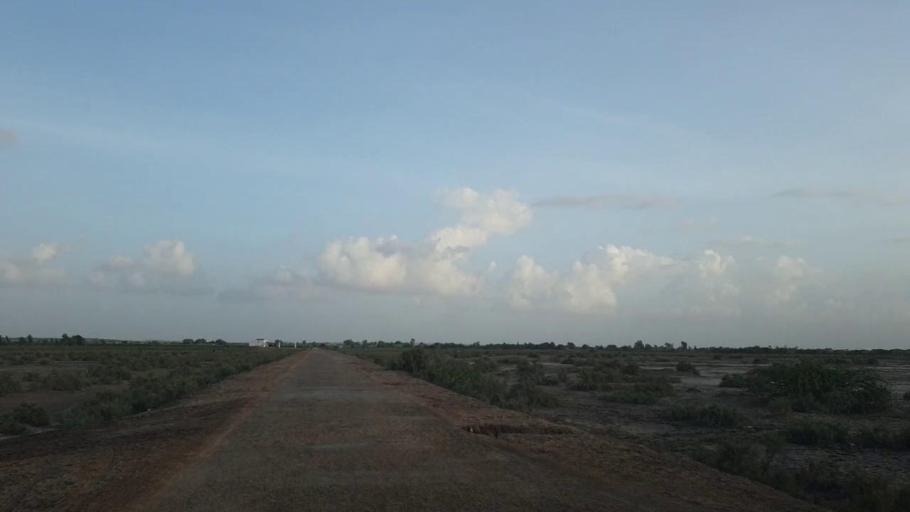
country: PK
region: Sindh
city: Kadhan
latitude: 24.5523
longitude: 69.1236
